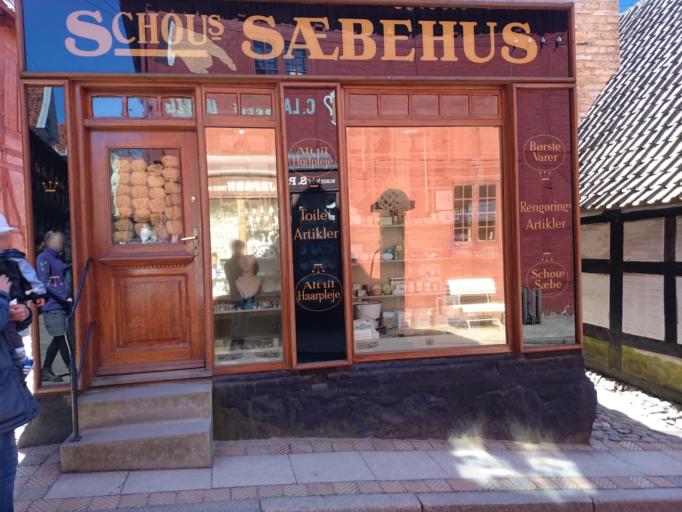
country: DK
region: Central Jutland
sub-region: Arhus Kommune
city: Arhus
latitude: 56.1589
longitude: 10.1928
